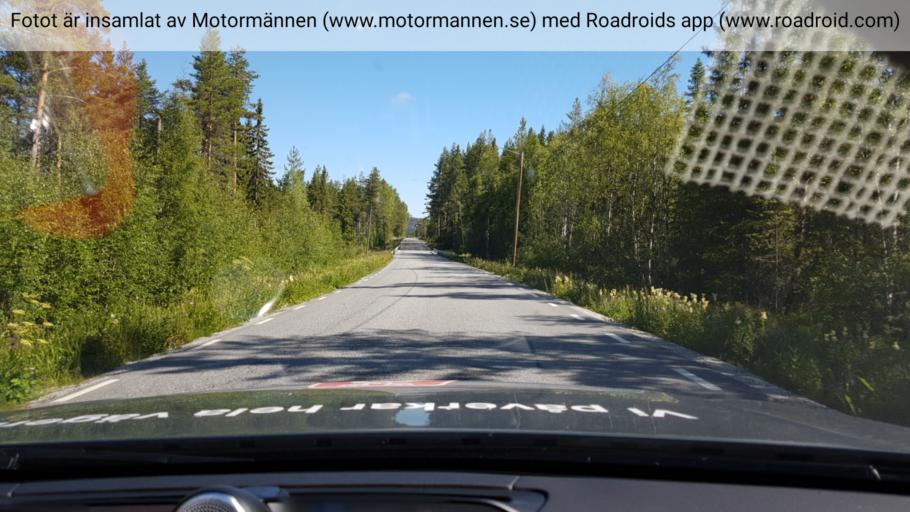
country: SE
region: Jaemtland
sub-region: Braecke Kommun
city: Braecke
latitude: 63.1486
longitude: 15.5475
